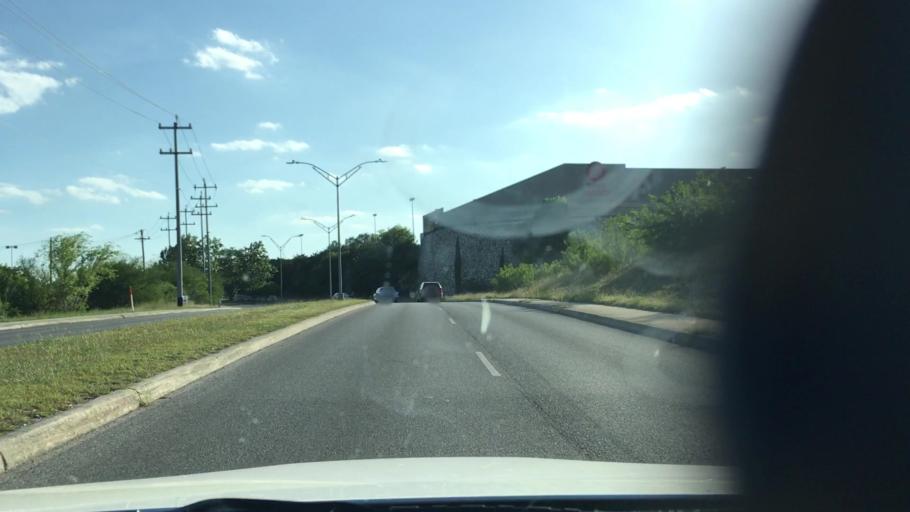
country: US
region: Texas
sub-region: Bexar County
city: Timberwood Park
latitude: 29.6537
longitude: -98.4426
